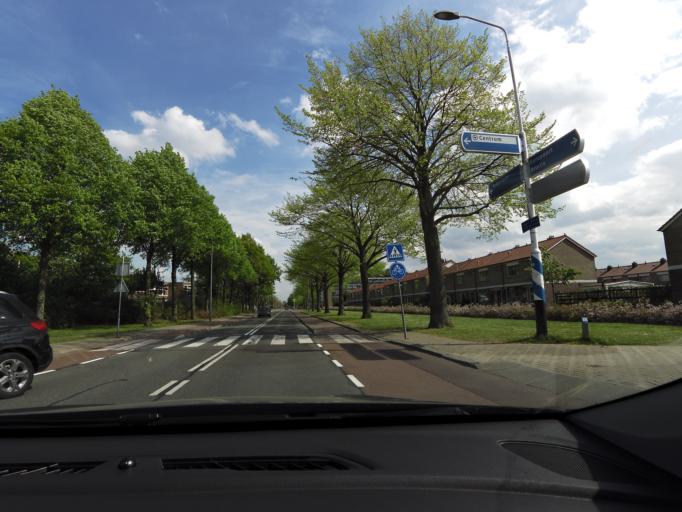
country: NL
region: South Holland
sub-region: Gemeente Maassluis
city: Maassluis
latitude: 51.9035
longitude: 4.2450
